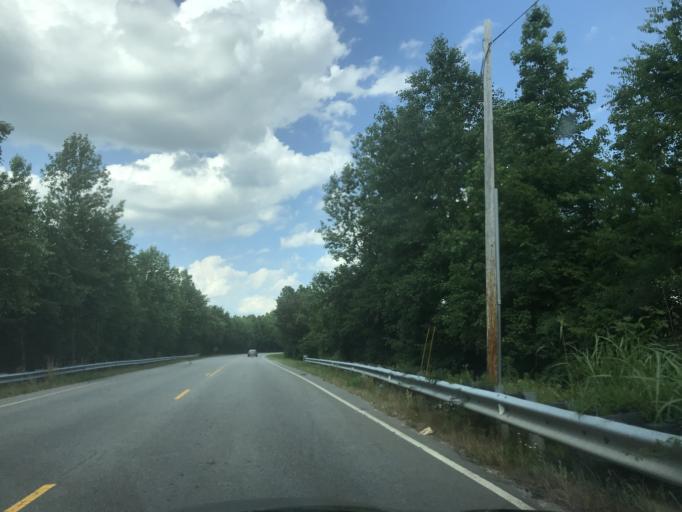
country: US
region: North Carolina
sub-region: Nash County
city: Spring Hope
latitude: 35.9284
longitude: -78.1477
